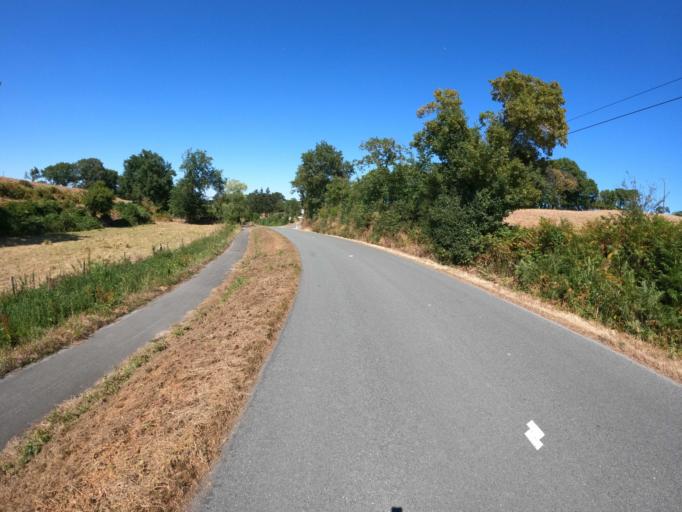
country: FR
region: Pays de la Loire
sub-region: Departement de la Vendee
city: Saint-Aubin-des-Ormeaux
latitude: 46.9990
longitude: -1.0255
